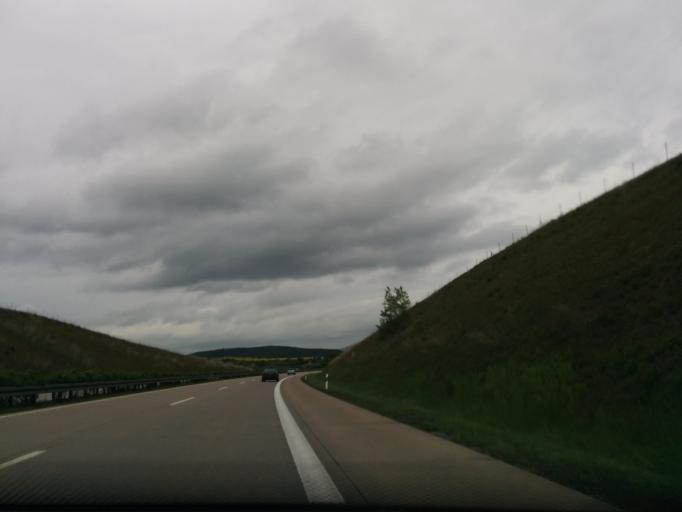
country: DE
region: Thuringia
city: Rohr
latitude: 50.5912
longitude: 10.4918
